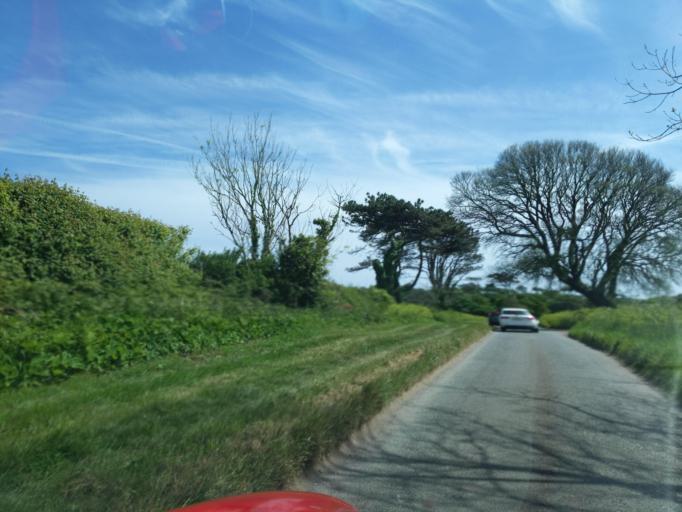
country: GB
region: England
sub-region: Devon
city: Dartmouth
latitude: 50.3612
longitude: -3.5484
